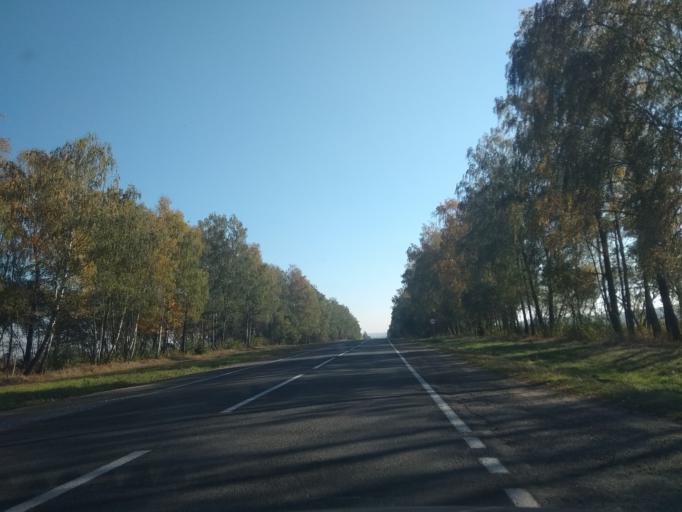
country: BY
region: Grodnenskaya
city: Slonim
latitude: 53.1222
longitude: 25.0917
